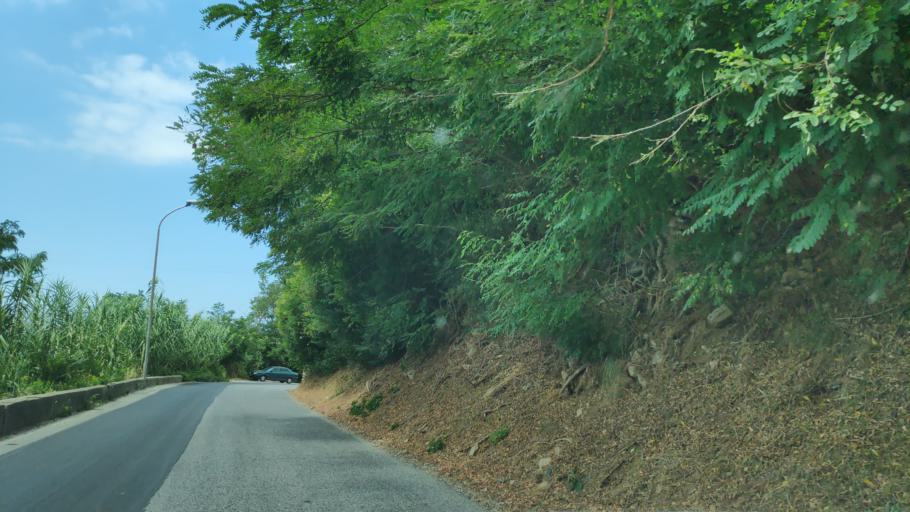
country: IT
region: Calabria
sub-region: Provincia di Cosenza
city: Paola
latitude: 39.3534
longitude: 16.0448
